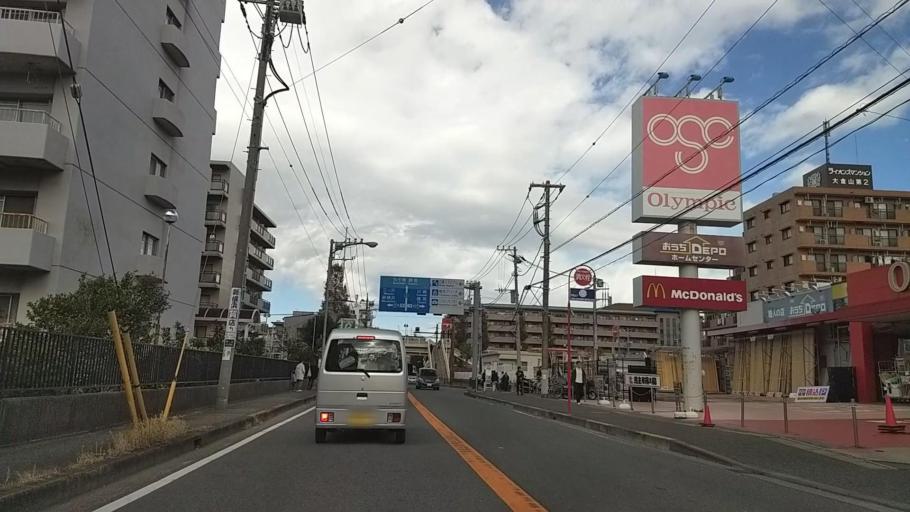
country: JP
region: Kanagawa
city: Yokohama
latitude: 35.5170
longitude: 139.6321
